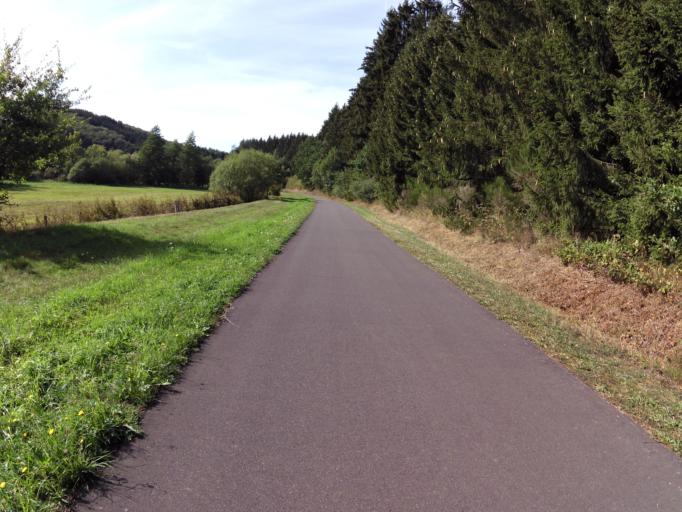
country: DE
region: Rheinland-Pfalz
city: Brandscheid
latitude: 50.1889
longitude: 6.3014
